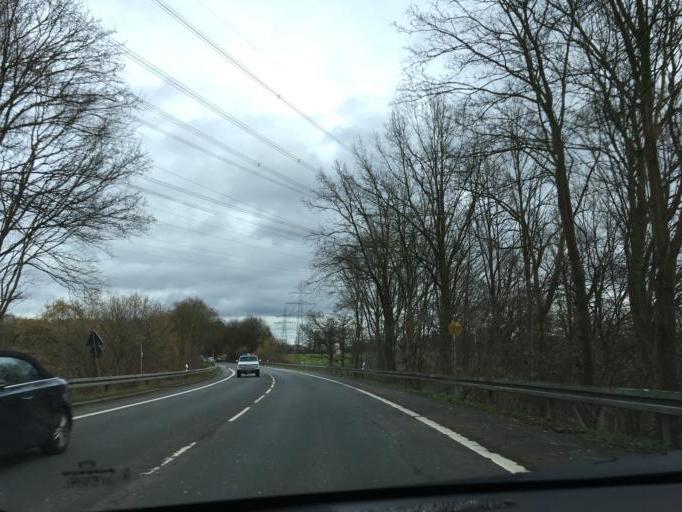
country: DE
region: North Rhine-Westphalia
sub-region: Regierungsbezirk Arnsberg
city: Dortmund
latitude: 51.4695
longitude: 7.4655
